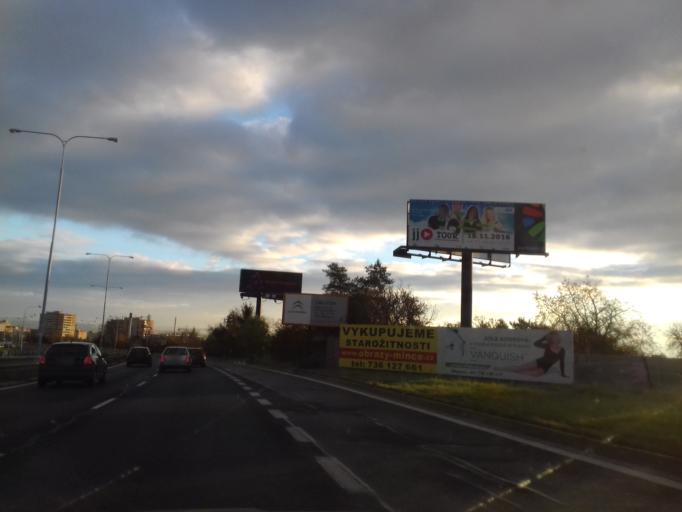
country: CZ
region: Olomoucky
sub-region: Okres Olomouc
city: Olomouc
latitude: 49.5730
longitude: 17.2331
